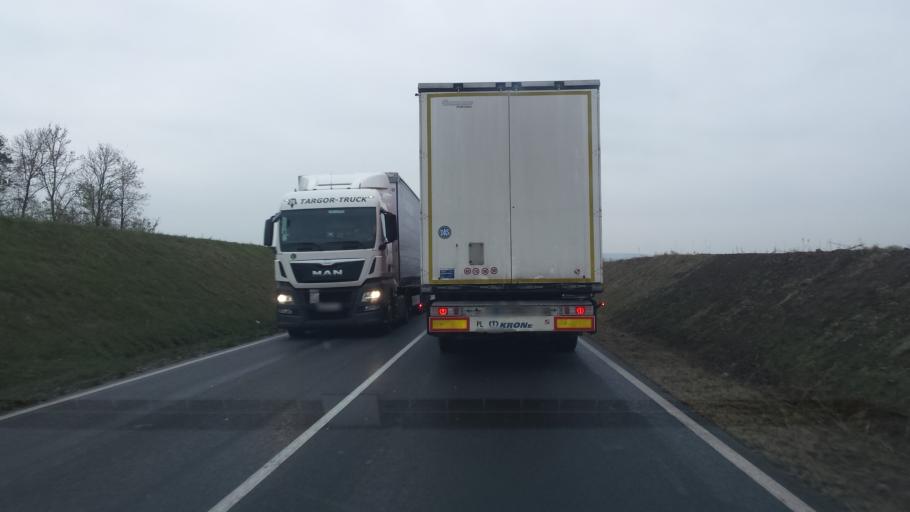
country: AT
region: Lower Austria
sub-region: Politischer Bezirk Mistelbach
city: Wilfersdorf
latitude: 48.5566
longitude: 16.6339
